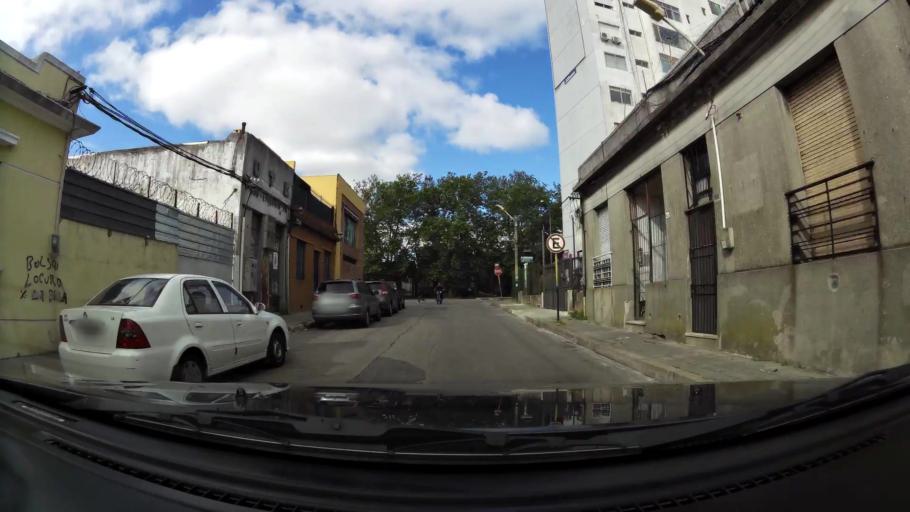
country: UY
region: Montevideo
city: Montevideo
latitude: -34.8797
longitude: -56.1466
